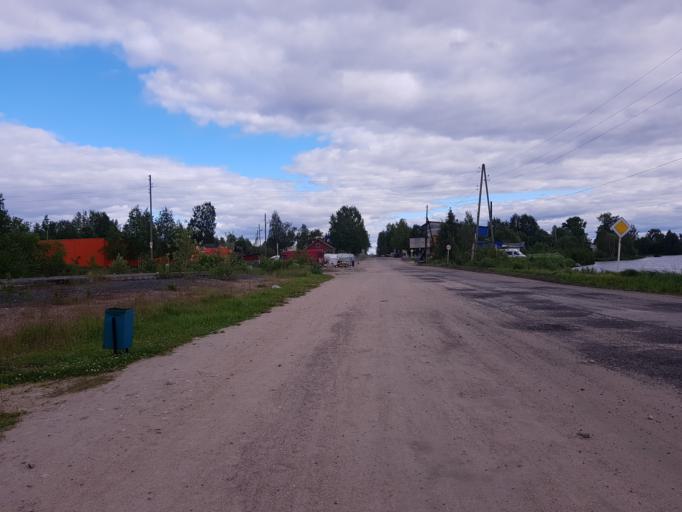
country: RU
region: Republic of Karelia
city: Kalevala
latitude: 65.1995
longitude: 31.1787
